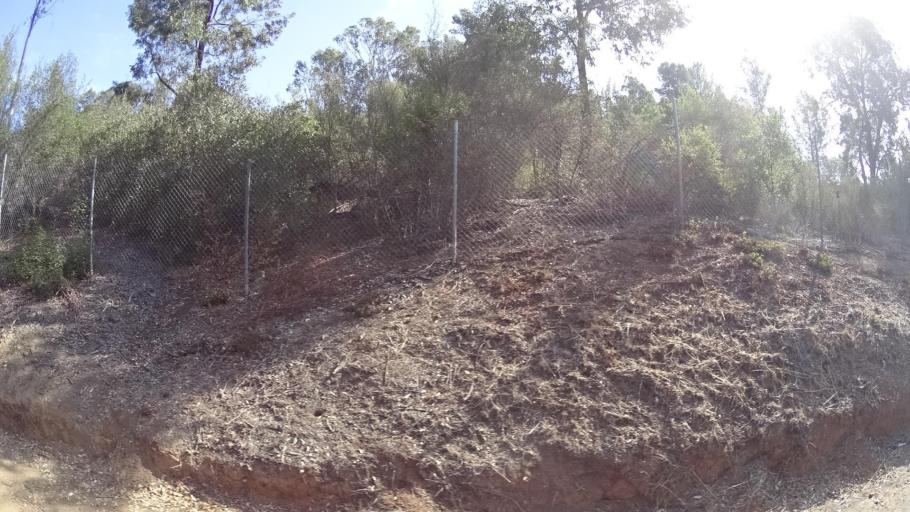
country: US
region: California
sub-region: San Diego County
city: San Marcos
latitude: 33.0890
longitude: -117.1651
